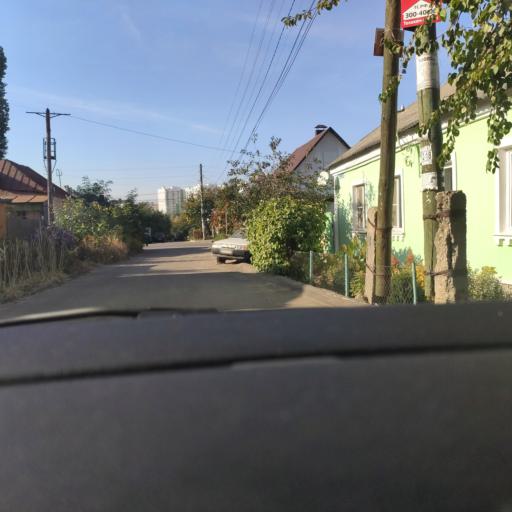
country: RU
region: Voronezj
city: Voronezh
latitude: 51.6825
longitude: 39.1427
